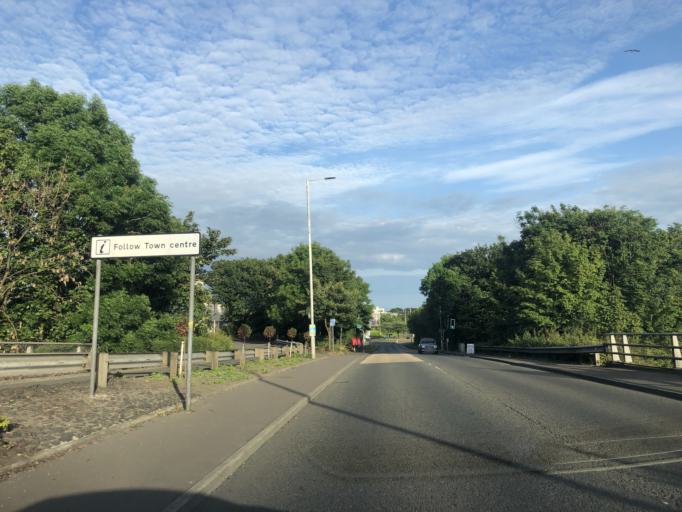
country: GB
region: Scotland
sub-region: Fife
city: Leven
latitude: 56.1974
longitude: -3.0069
